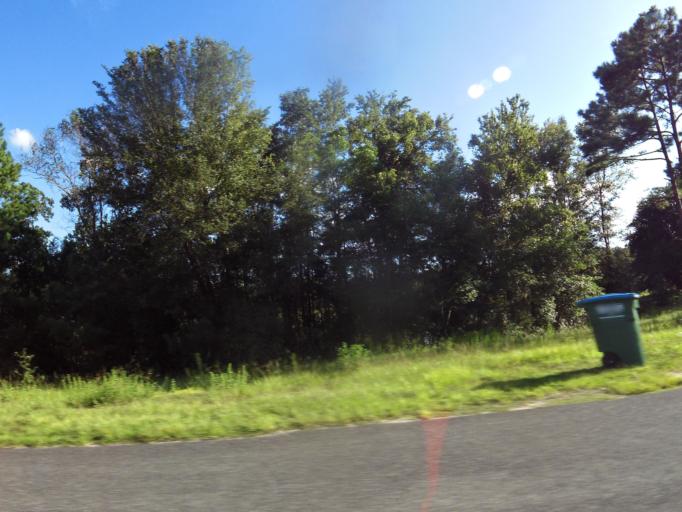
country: US
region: Florida
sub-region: Wakulla County
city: Crawfordville
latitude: 30.0639
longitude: -84.5071
